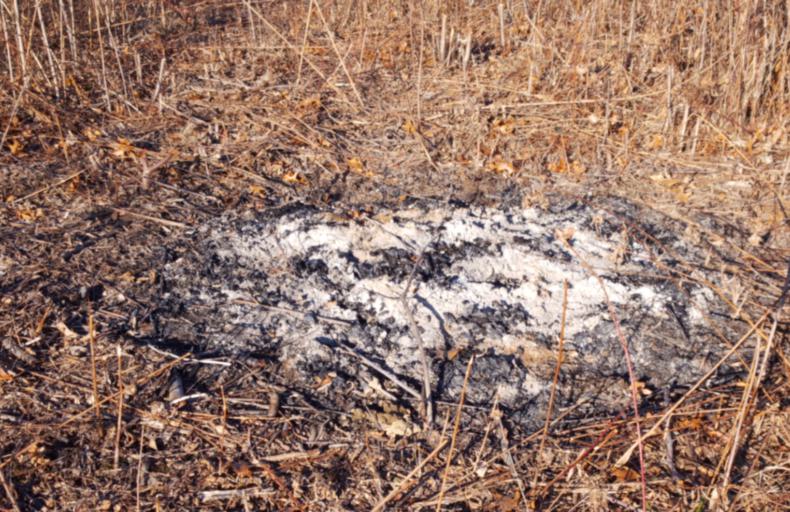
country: US
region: Illinois
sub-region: Cook County
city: Northbrook
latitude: 42.1395
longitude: -87.8274
